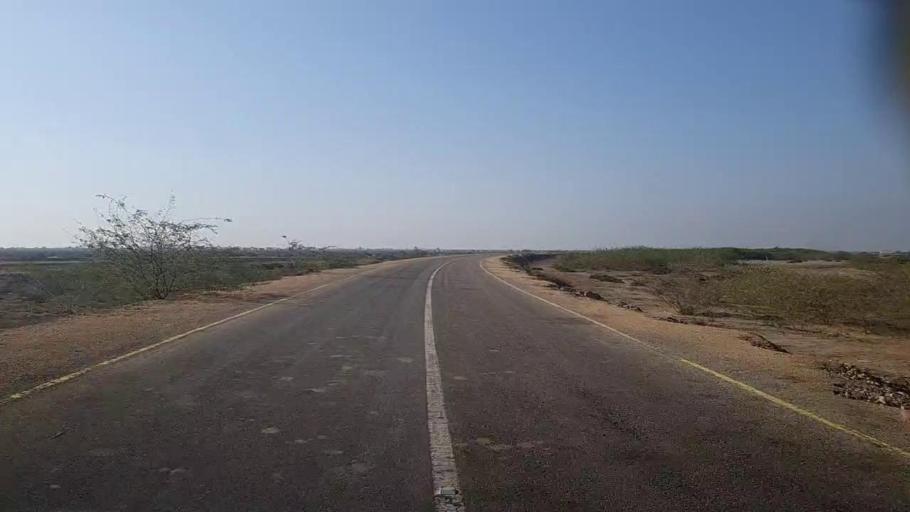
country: PK
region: Sindh
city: Mirpur Sakro
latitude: 24.5610
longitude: 67.4991
